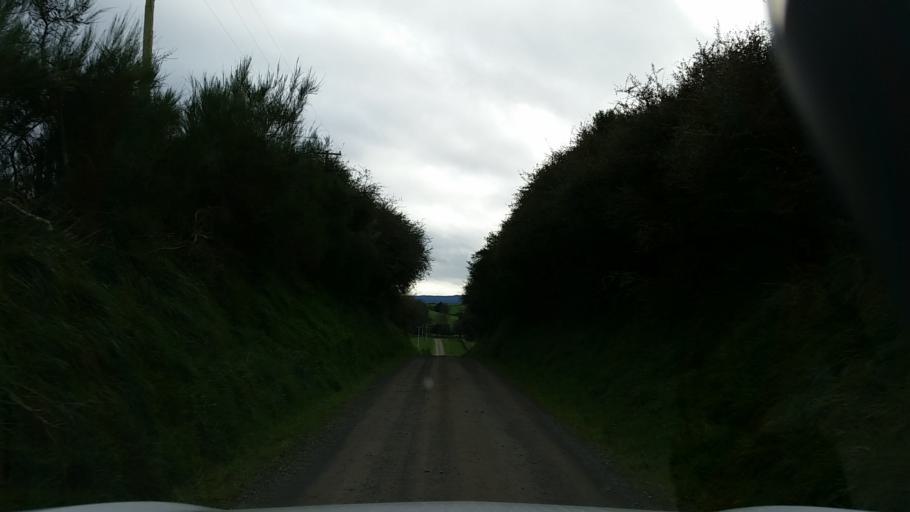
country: NZ
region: Bay of Plenty
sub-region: Whakatane District
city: Murupara
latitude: -38.3082
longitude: 176.4688
